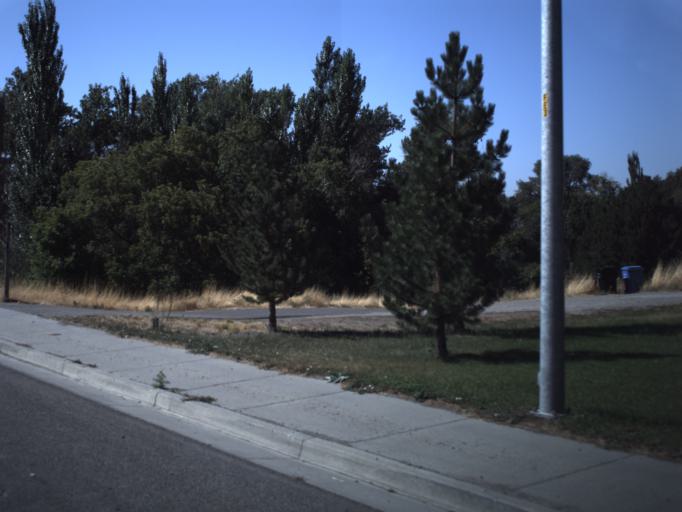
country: US
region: Utah
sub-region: Cache County
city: Hyrum
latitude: 41.6413
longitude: -111.8328
